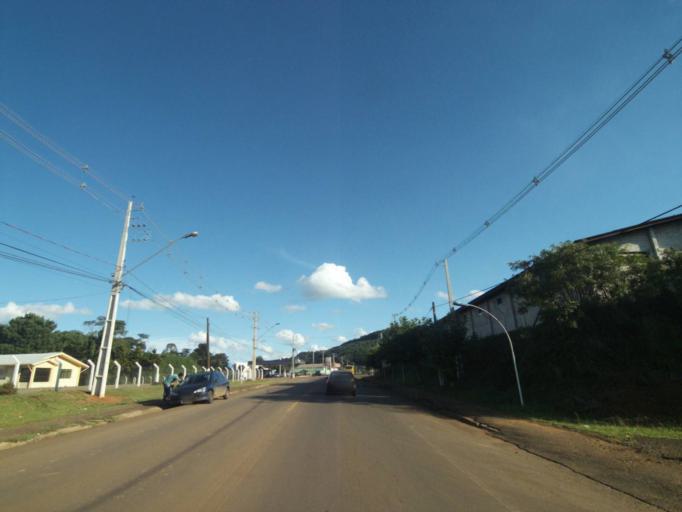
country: BR
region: Parana
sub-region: Uniao Da Vitoria
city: Uniao da Vitoria
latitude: -26.1622
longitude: -51.5375
